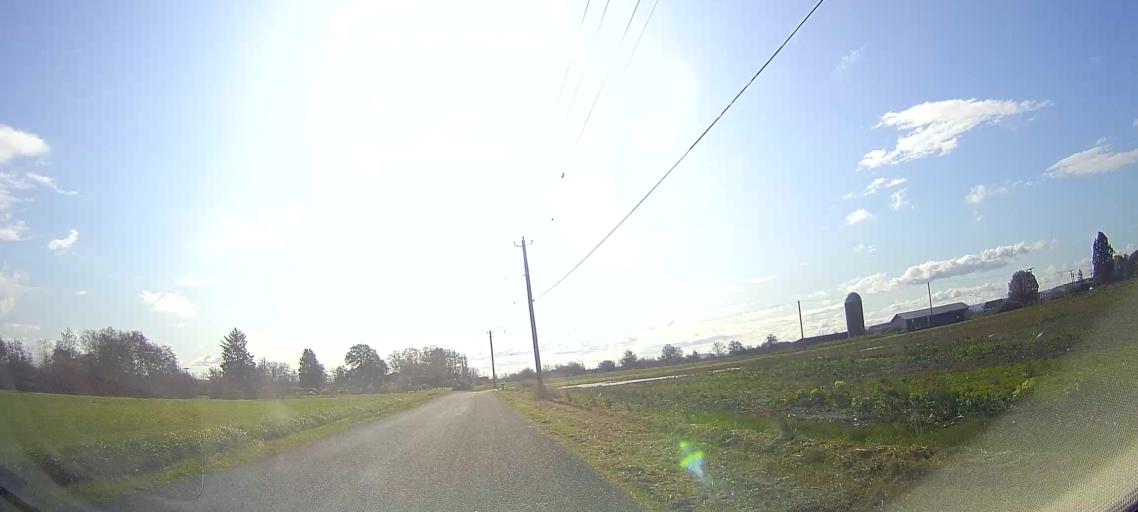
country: US
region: Washington
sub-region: Snohomish County
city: Stanwood
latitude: 48.3281
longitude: -122.3788
